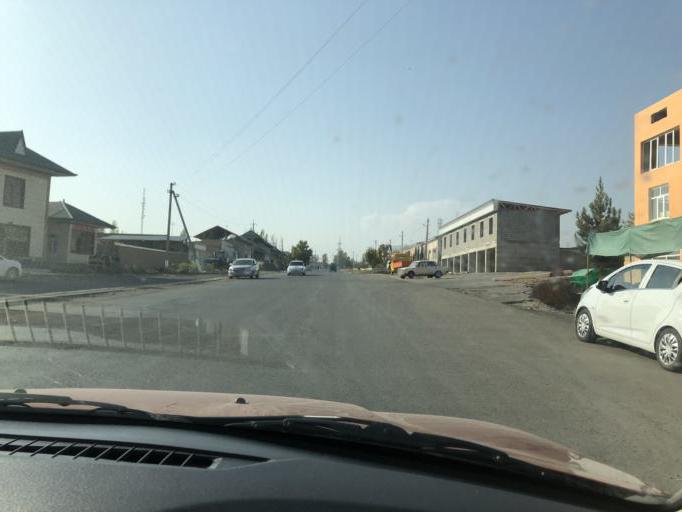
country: UZ
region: Namangan
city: Chust Shahri
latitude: 41.0735
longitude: 71.2037
